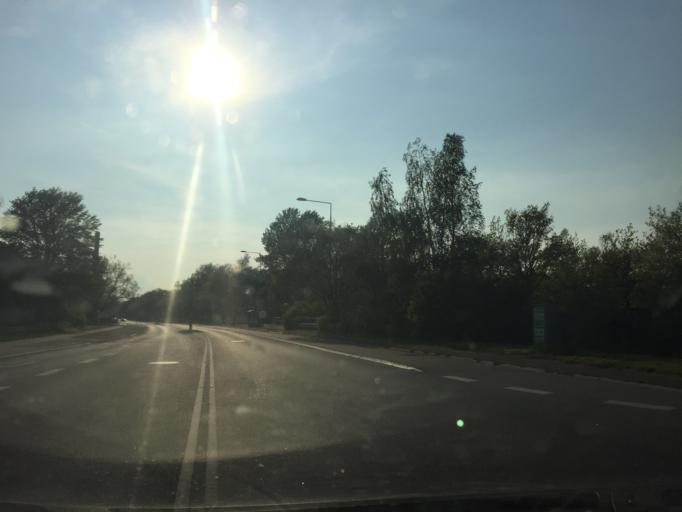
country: DK
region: Capital Region
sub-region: Hoje-Taastrup Kommune
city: Taastrup
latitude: 55.6557
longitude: 12.2979
